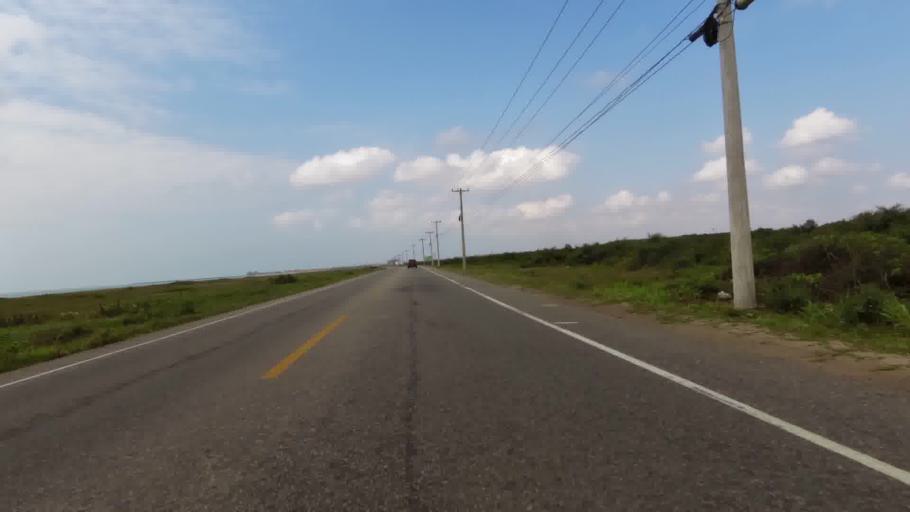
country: BR
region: Espirito Santo
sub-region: Itapemirim
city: Itapemirim
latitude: -20.9753
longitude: -40.8116
